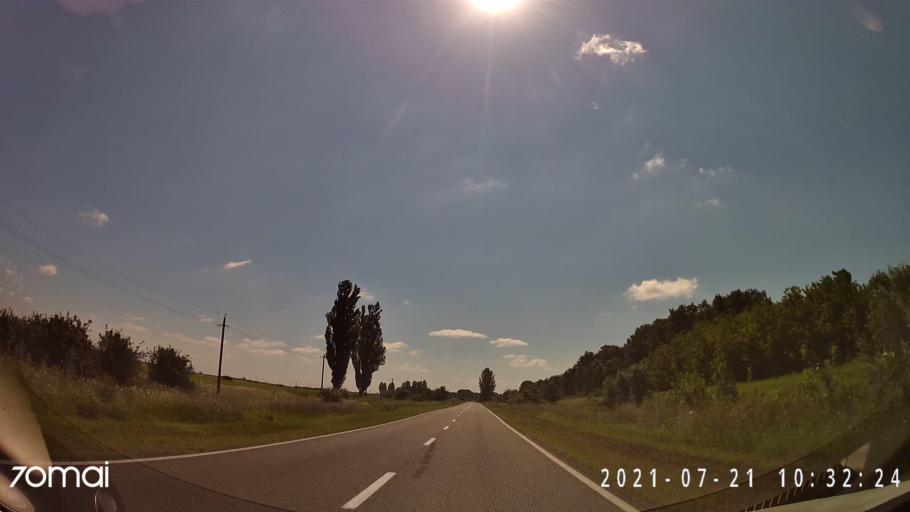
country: RO
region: Tulcea
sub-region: Oras Isaccea
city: Isaccea
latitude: 45.3019
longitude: 28.4229
